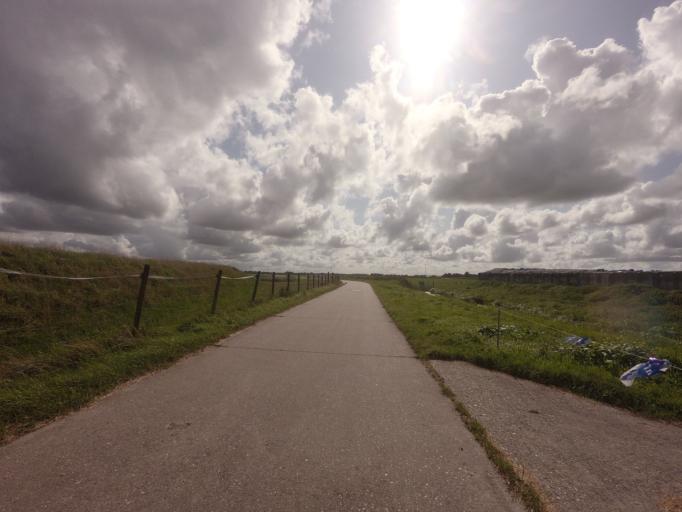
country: NL
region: Friesland
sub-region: Sudwest Fryslan
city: Scharnegoutum
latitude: 53.0712
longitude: 5.6373
